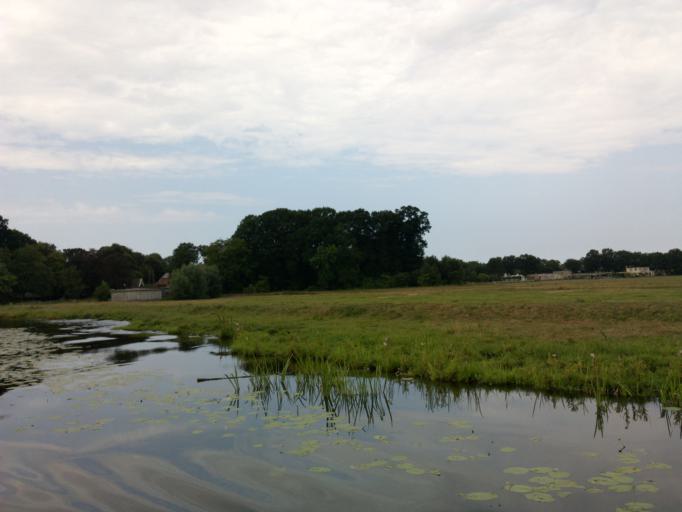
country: NL
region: South Holland
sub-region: Gemeente Teylingen
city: Sassenheim
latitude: 52.2276
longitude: 4.5371
